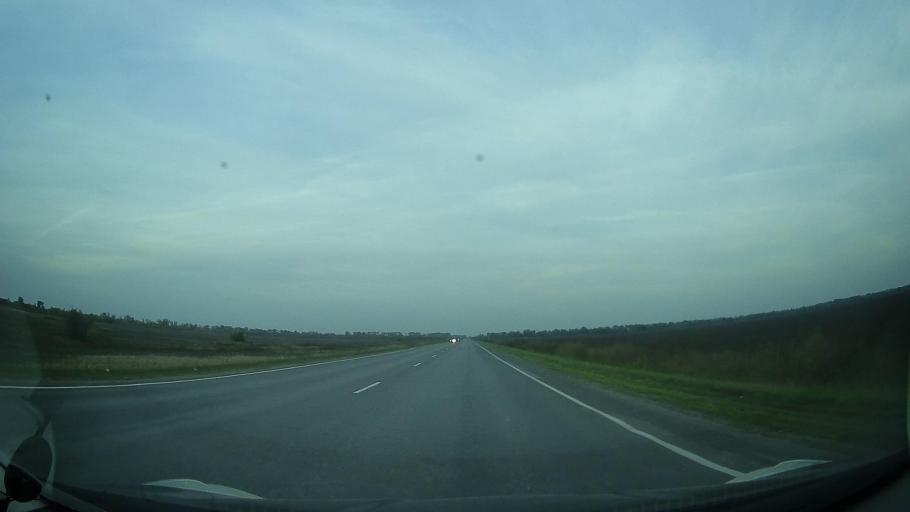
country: RU
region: Rostov
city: Ol'ginskaya
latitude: 47.1300
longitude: 39.9136
